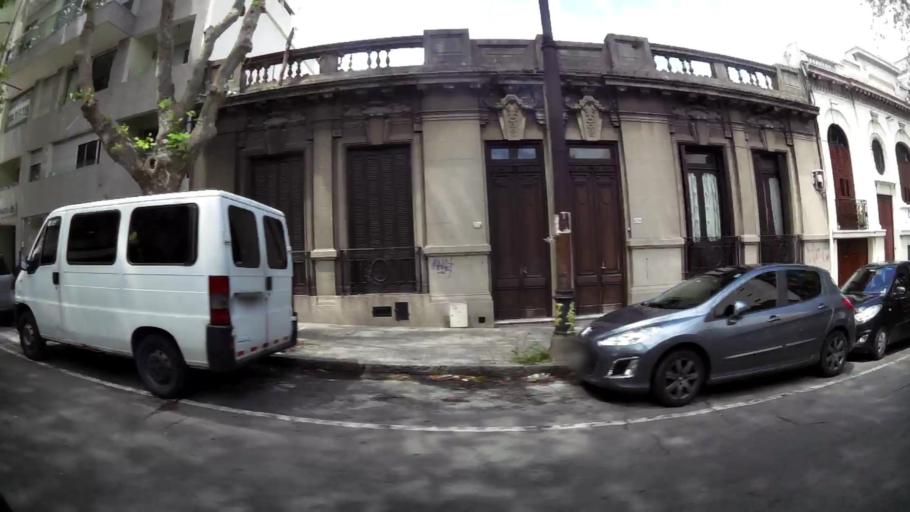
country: UY
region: Montevideo
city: Montevideo
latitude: -34.9068
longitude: -56.1643
